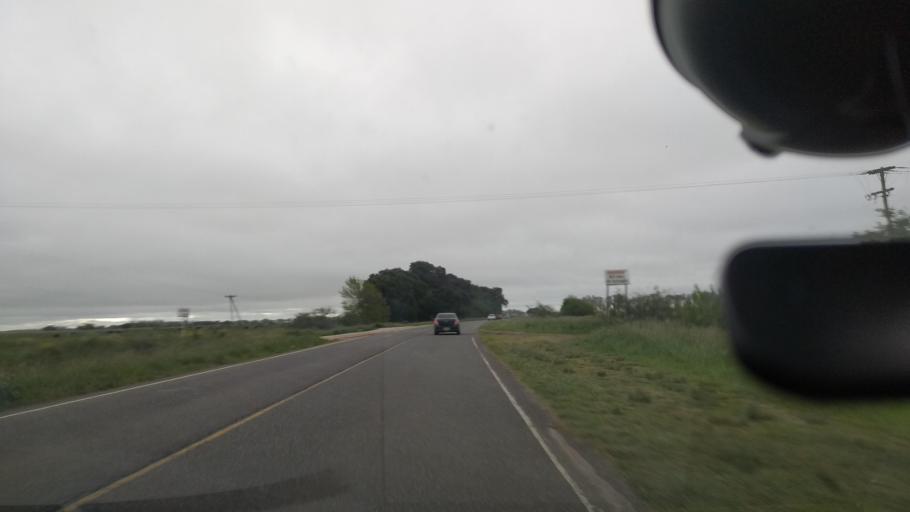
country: AR
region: Buenos Aires
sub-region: Partido de Magdalena
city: Magdalena
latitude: -35.1993
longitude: -57.7808
